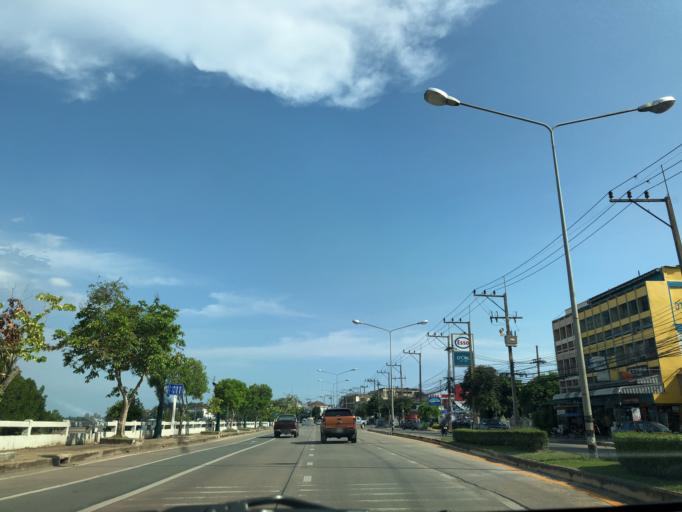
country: TH
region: Krabi
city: Krabi
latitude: 8.0710
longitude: 98.9167
